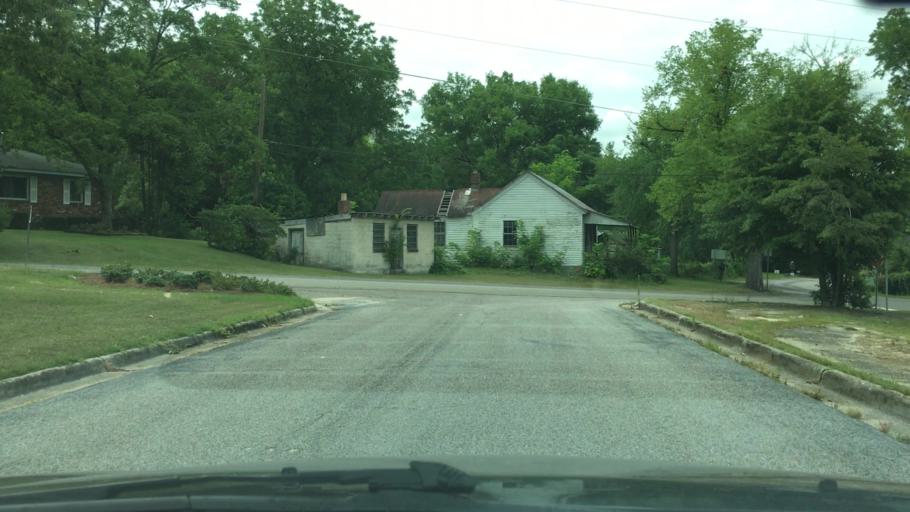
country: US
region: South Carolina
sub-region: Aiken County
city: Graniteville
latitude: 33.5609
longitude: -81.8033
